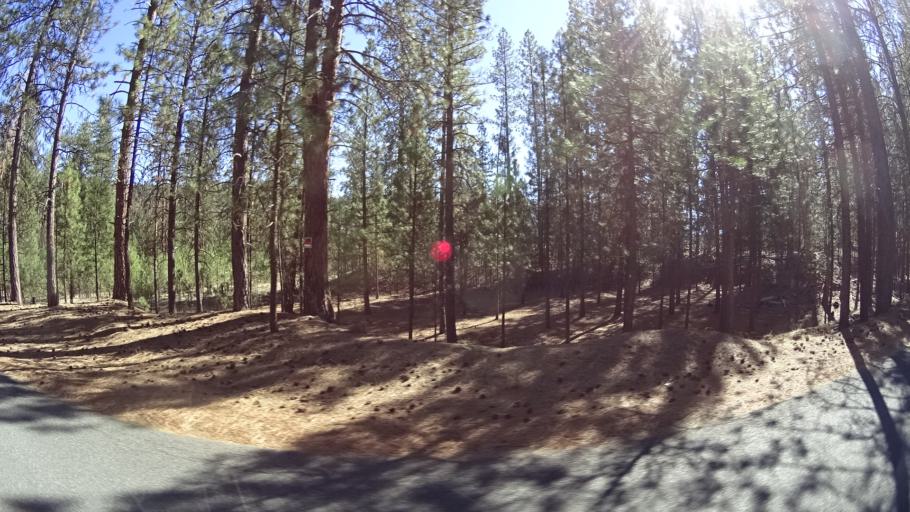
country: US
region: California
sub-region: Siskiyou County
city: Yreka
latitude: 41.5818
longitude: -122.9147
